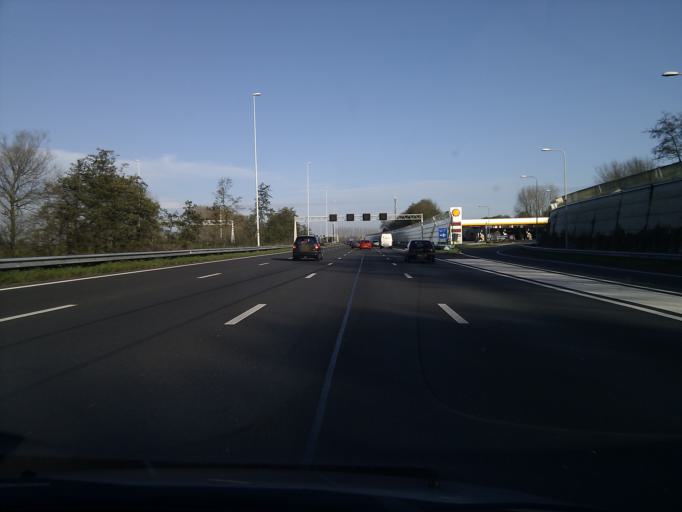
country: NL
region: South Holland
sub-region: Gemeente Gouda
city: Bloemendaal
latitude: 52.0386
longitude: 4.7025
